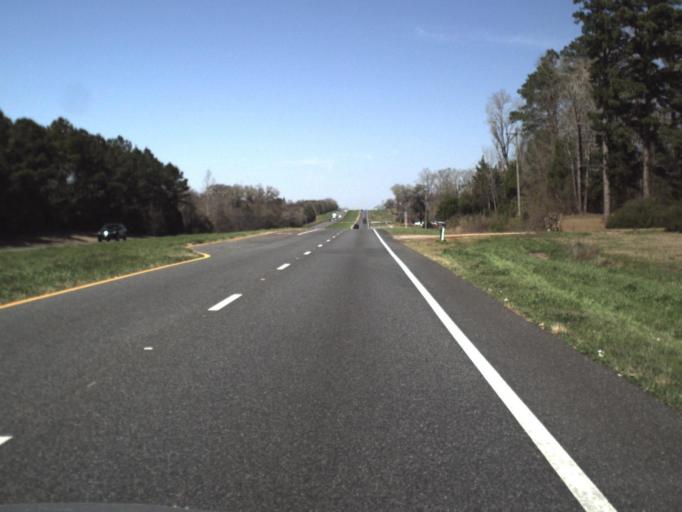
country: US
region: Florida
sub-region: Jackson County
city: Marianna
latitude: 30.8762
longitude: -85.3624
